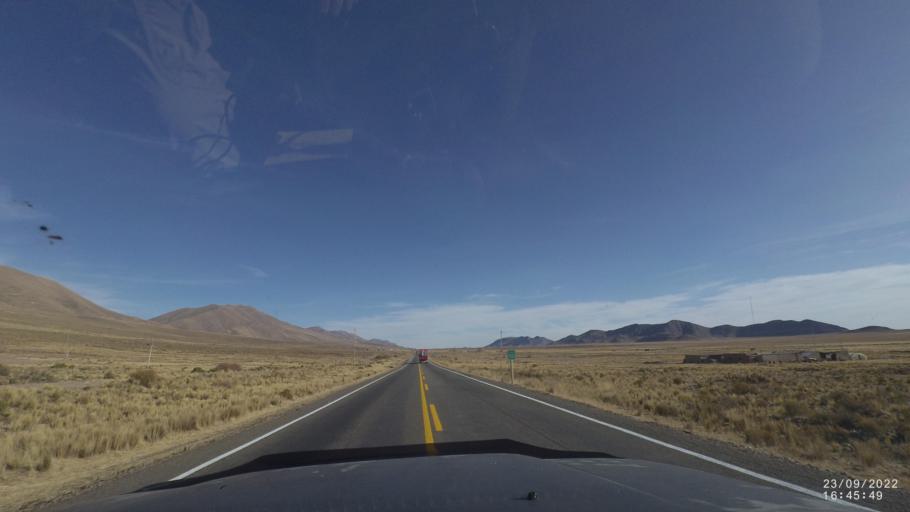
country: BO
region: Oruro
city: Poopo
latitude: -18.3468
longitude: -66.9850
